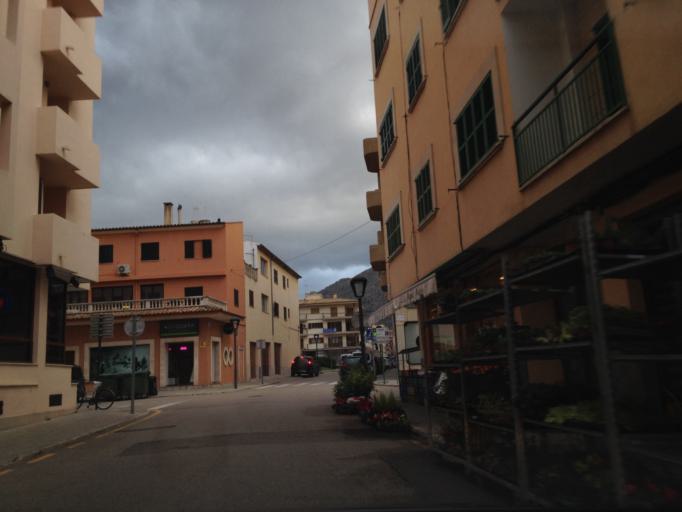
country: ES
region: Balearic Islands
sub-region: Illes Balears
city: Pollenca
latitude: 39.8768
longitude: 3.0199
